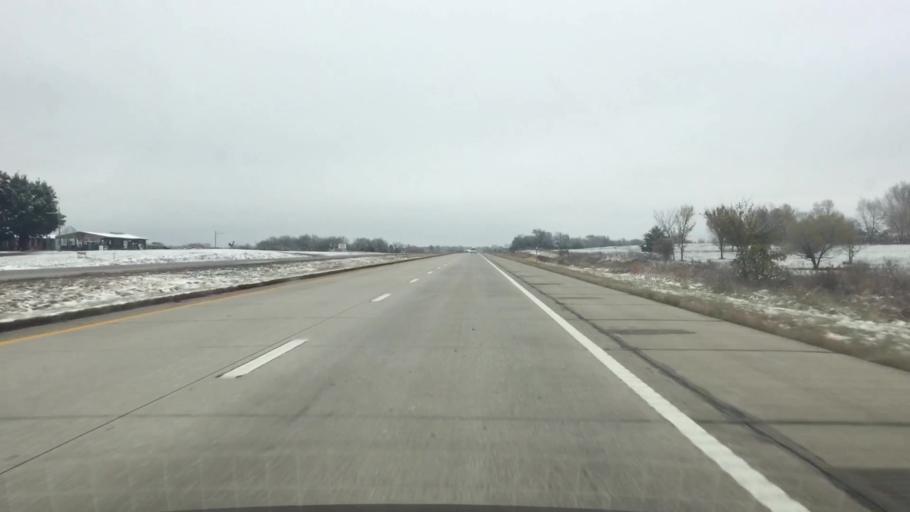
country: US
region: Missouri
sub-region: Saint Clair County
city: Osceola
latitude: 38.1839
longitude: -93.7324
